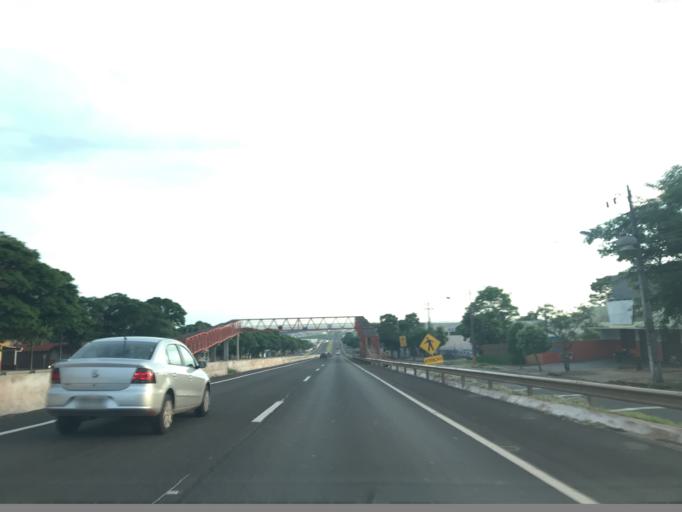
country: BR
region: Parana
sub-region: Maringa
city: Maringa
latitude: -23.4007
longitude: -51.9789
